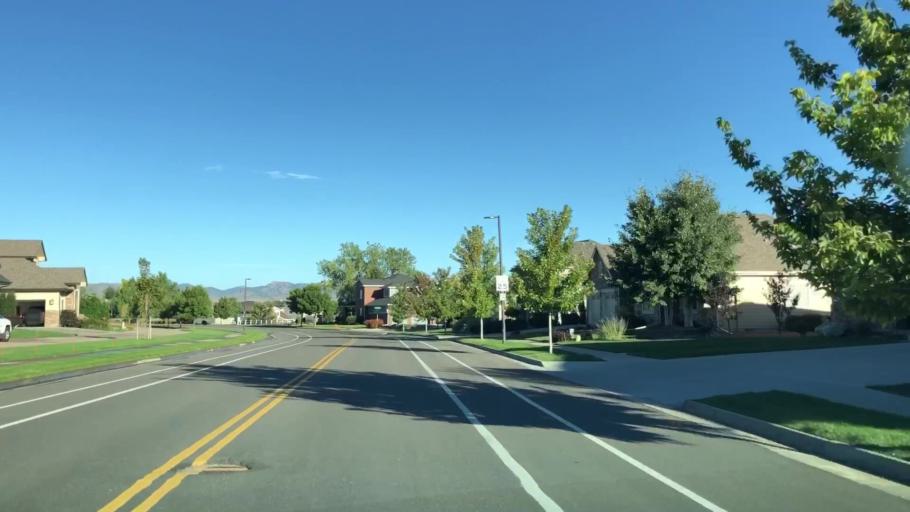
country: US
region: Colorado
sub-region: Larimer County
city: Loveland
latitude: 40.4532
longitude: -105.0277
